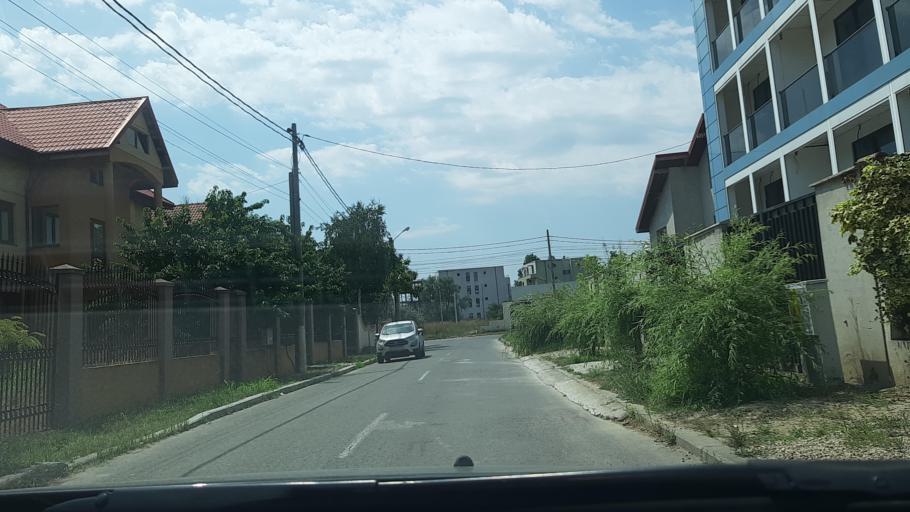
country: RO
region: Constanta
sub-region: Comuna Navodari
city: Navodari
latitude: 44.3009
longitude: 28.6218
